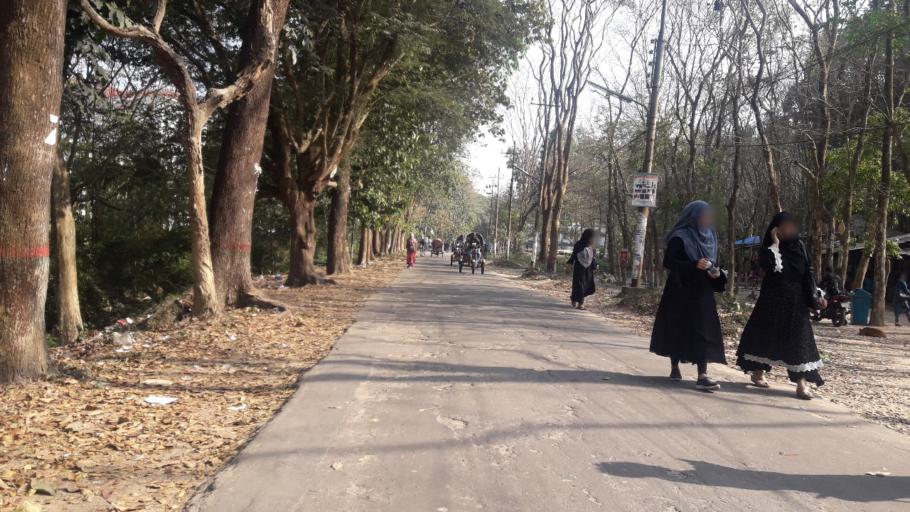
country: BD
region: Chittagong
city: Chittagong
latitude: 22.4703
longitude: 91.7872
